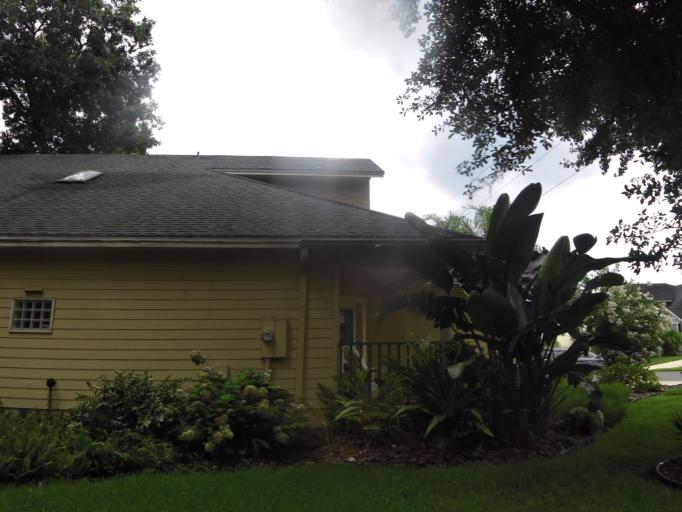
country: US
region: Florida
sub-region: Duval County
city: Atlantic Beach
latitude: 30.3360
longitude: -81.4249
